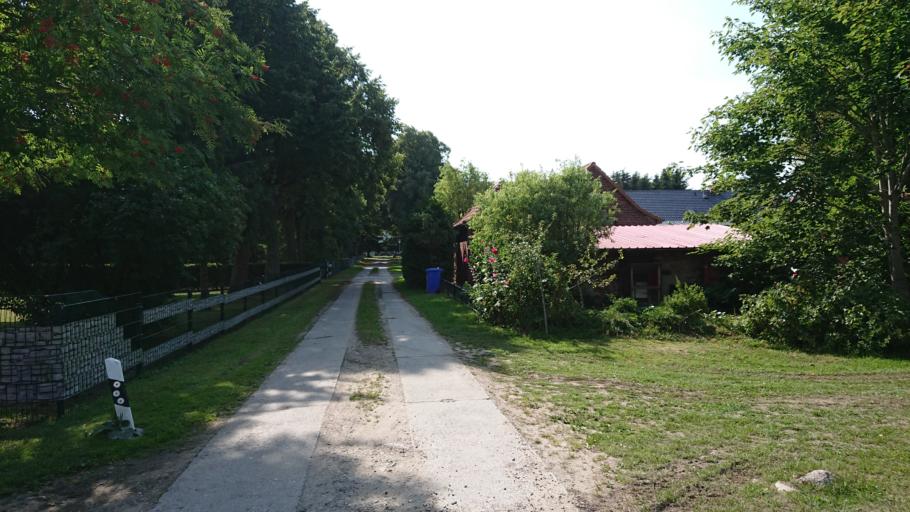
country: DE
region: Mecklenburg-Vorpommern
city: Gormin
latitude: 53.9821
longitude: 13.2846
